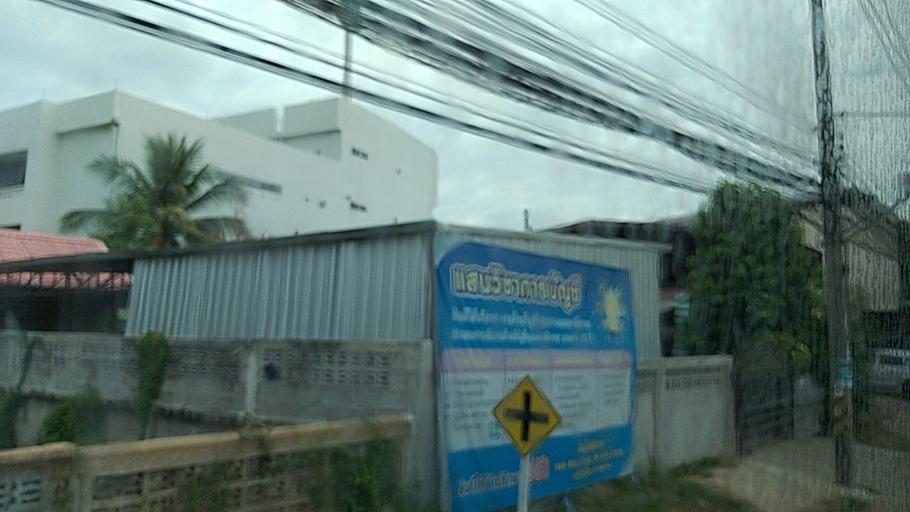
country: TH
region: Maha Sarakham
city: Kantharawichai
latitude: 16.3251
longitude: 103.2982
